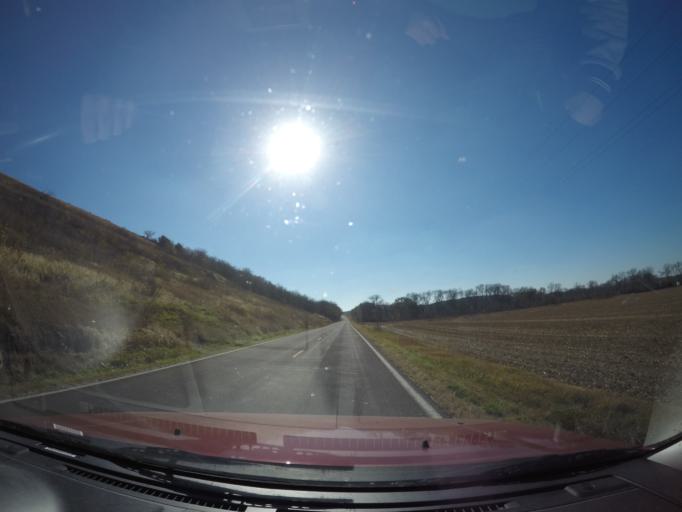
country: US
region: Kansas
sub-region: Geary County
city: Grandview Plaza
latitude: 39.0022
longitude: -96.7305
